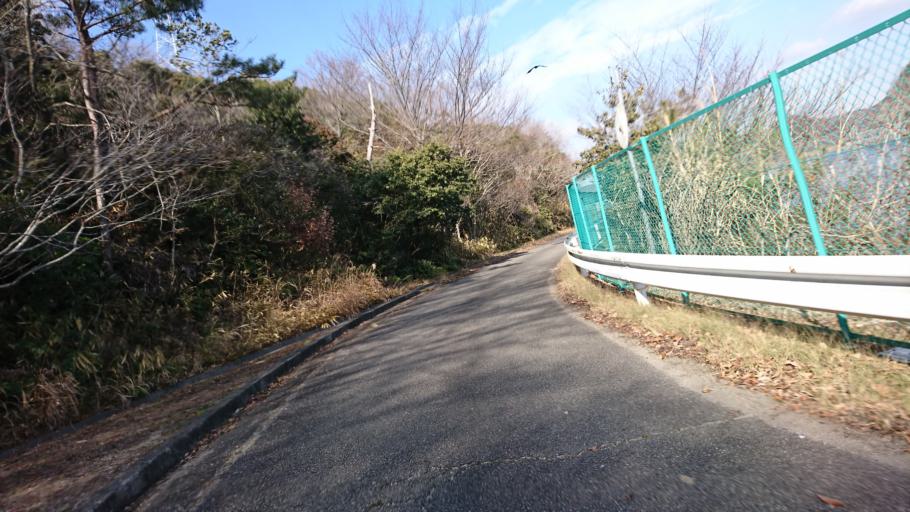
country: JP
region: Hyogo
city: Kakogawacho-honmachi
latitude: 34.8192
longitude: 134.8729
